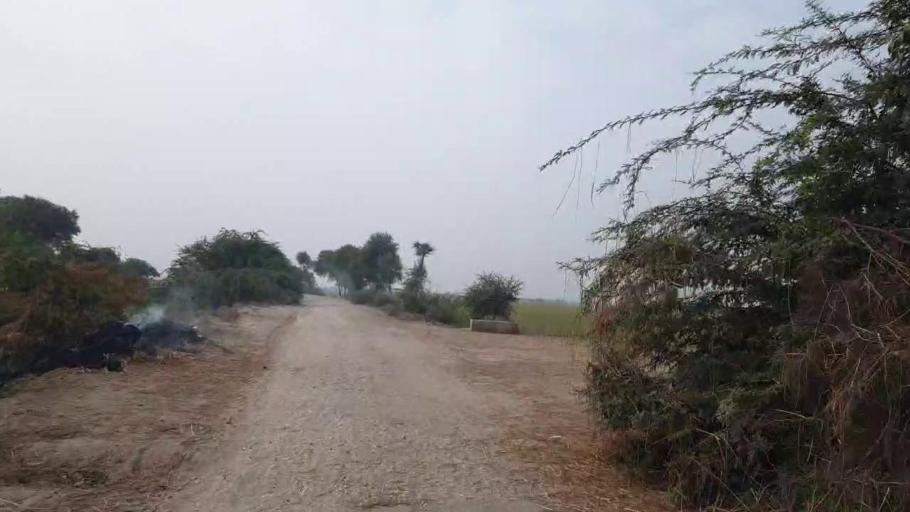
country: PK
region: Sindh
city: Kario
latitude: 24.8995
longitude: 68.5281
